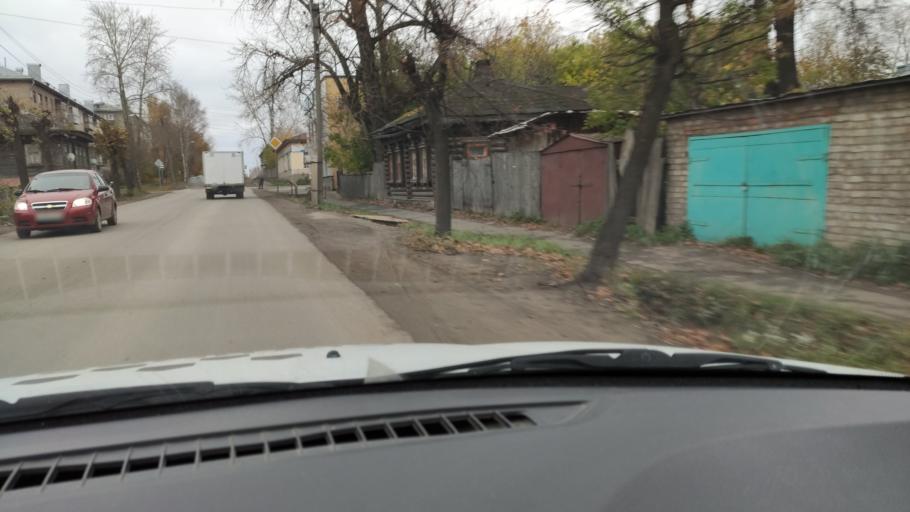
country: RU
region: Kirov
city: Slobodskoy
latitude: 58.7263
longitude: 50.1745
